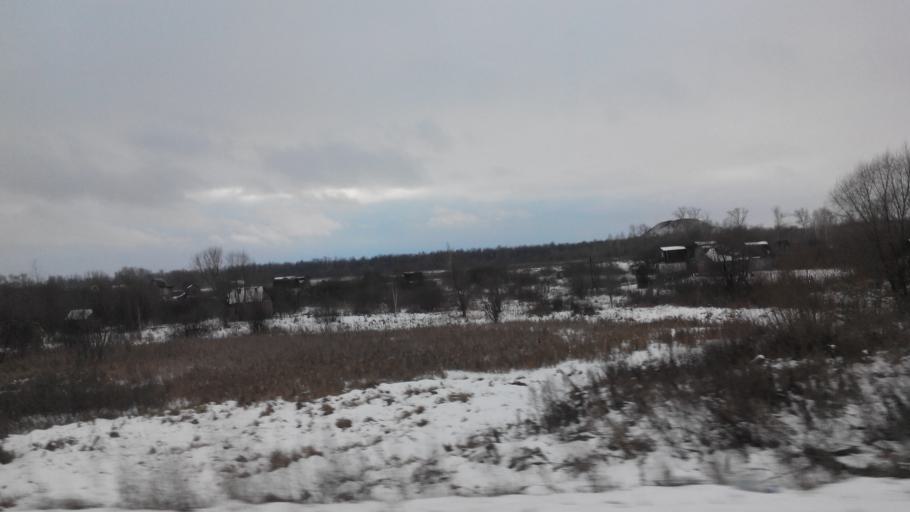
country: RU
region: Tula
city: Podlesnyy
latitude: 53.9693
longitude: 38.2593
